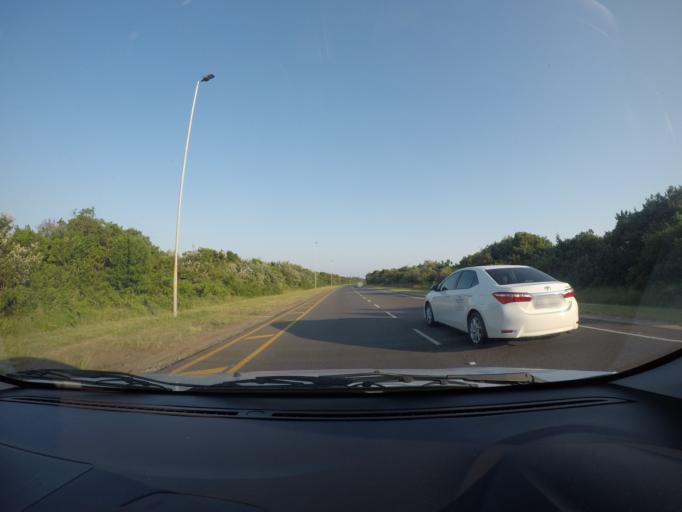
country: ZA
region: KwaZulu-Natal
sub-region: uThungulu District Municipality
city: Richards Bay
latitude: -28.7770
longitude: 32.0777
